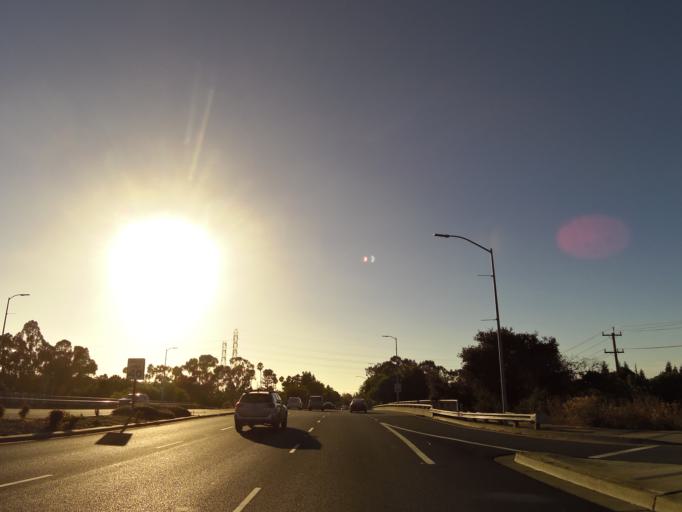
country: US
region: California
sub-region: Santa Clara County
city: Mountain View
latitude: 37.3780
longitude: -122.0668
